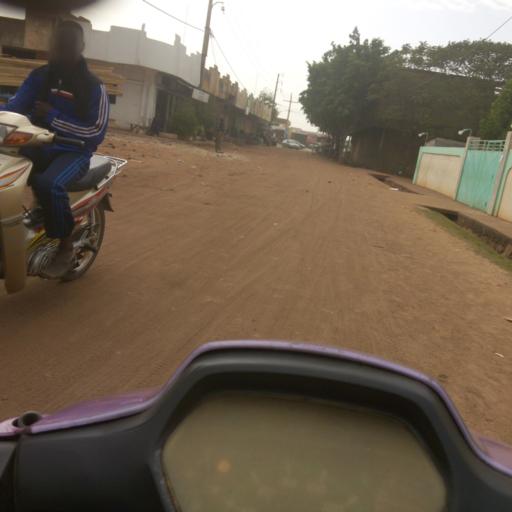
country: ML
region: Bamako
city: Bamako
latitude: 12.6647
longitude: -7.9450
